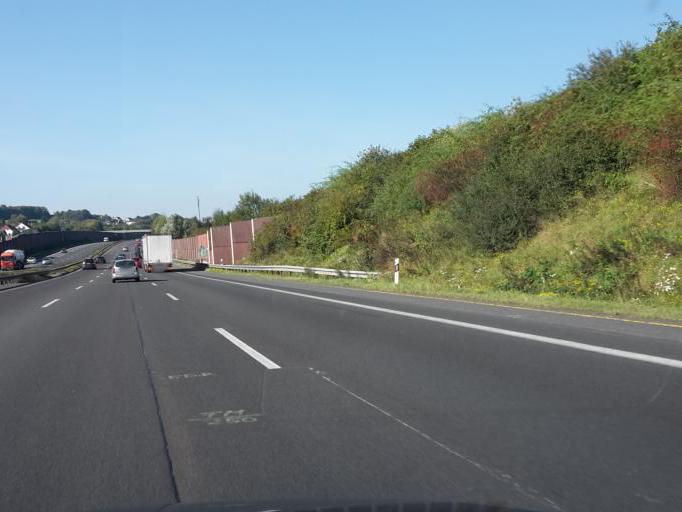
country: DE
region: North Rhine-Westphalia
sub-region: Regierungsbezirk Koln
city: Bad Honnef
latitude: 50.7019
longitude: 7.2573
